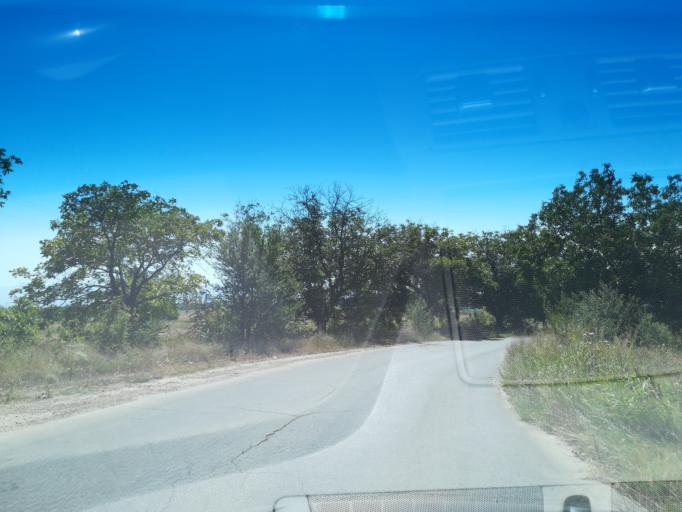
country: BG
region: Pazardzhik
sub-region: Obshtina Pazardzhik
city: Pazardzhik
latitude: 42.2941
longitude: 24.3985
